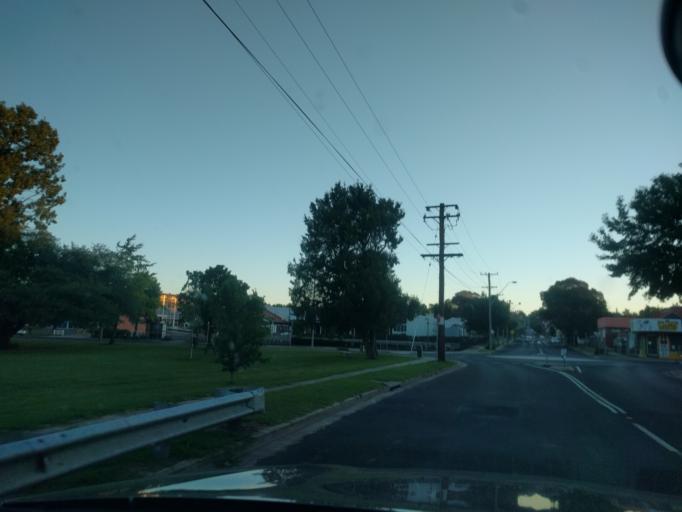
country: AU
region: New South Wales
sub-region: Armidale Dumaresq
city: Armidale
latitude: -30.5110
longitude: 151.6594
